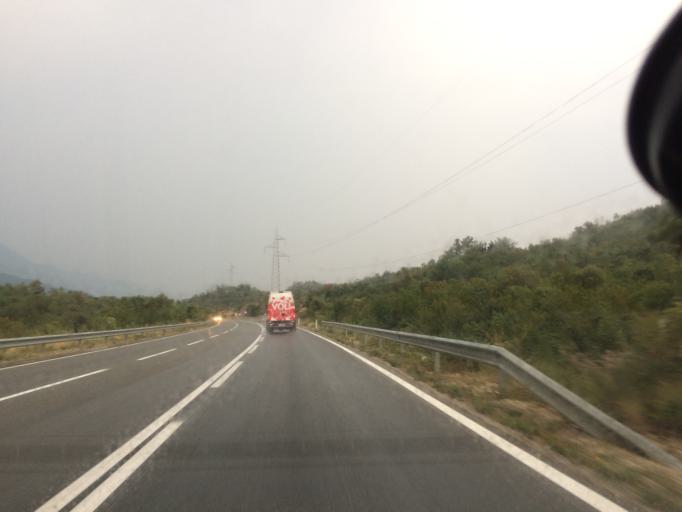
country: ME
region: Opstina Niksic
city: Niksic
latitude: 42.7114
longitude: 18.9518
